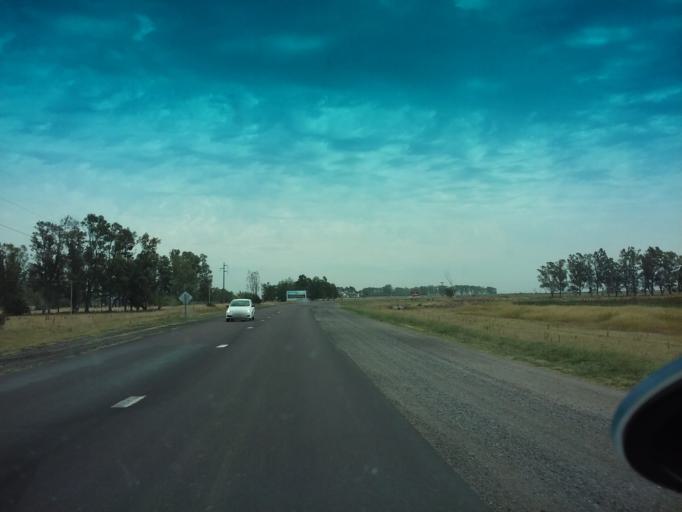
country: AR
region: Buenos Aires
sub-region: Partido de Pehuajo
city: Pehuajo
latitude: -35.8650
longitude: -62.2994
